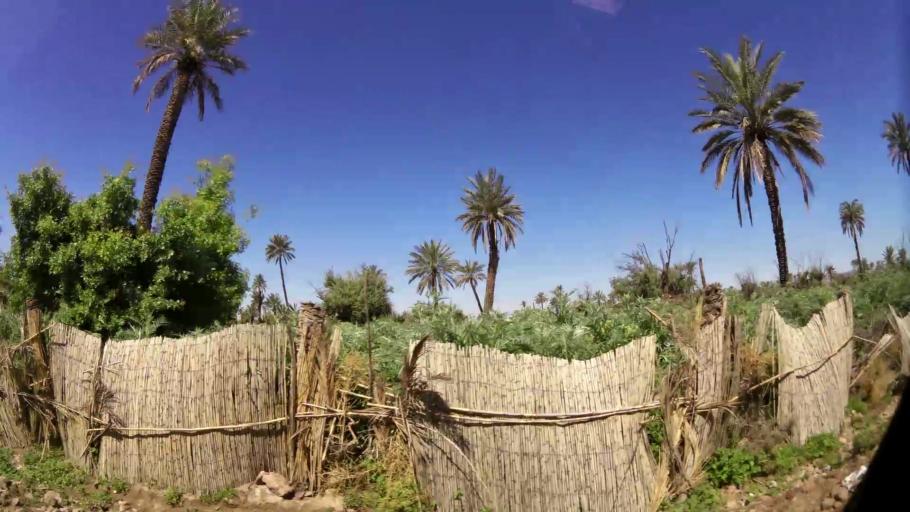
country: MA
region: Marrakech-Tensift-Al Haouz
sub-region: Marrakech
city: Marrakesh
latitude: 31.6780
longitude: -7.9801
